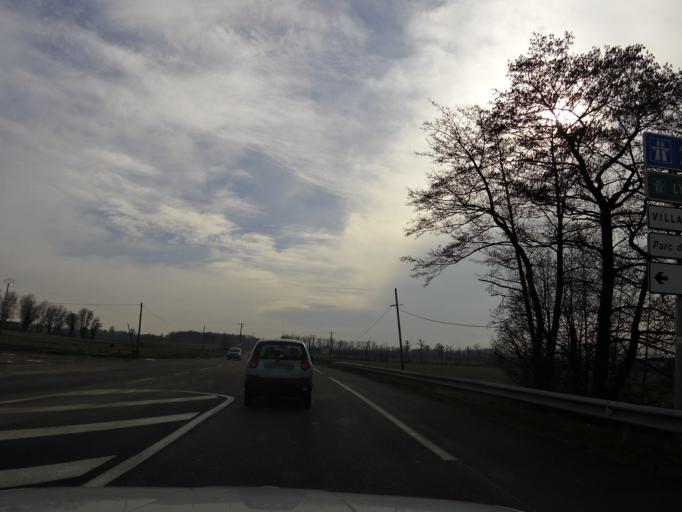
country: FR
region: Rhone-Alpes
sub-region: Departement de l'Ain
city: Villars-les-Dombes
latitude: 46.0497
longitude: 5.0709
